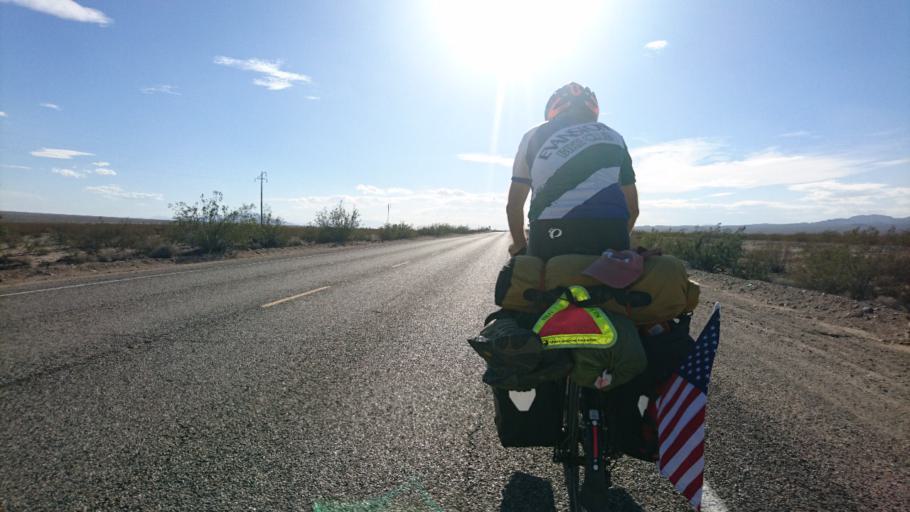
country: US
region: California
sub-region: San Bernardino County
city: Needles
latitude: 34.7128
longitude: -115.2806
